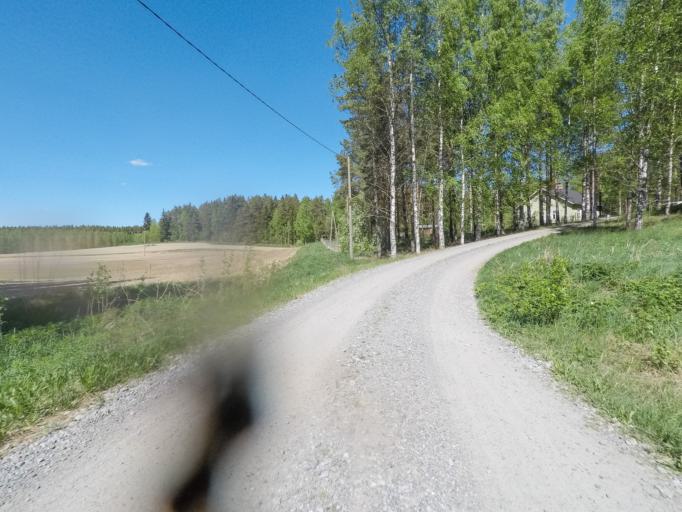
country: FI
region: Pirkanmaa
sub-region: Etelae-Pirkanmaa
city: Kylmaekoski
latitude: 61.1621
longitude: 23.7111
